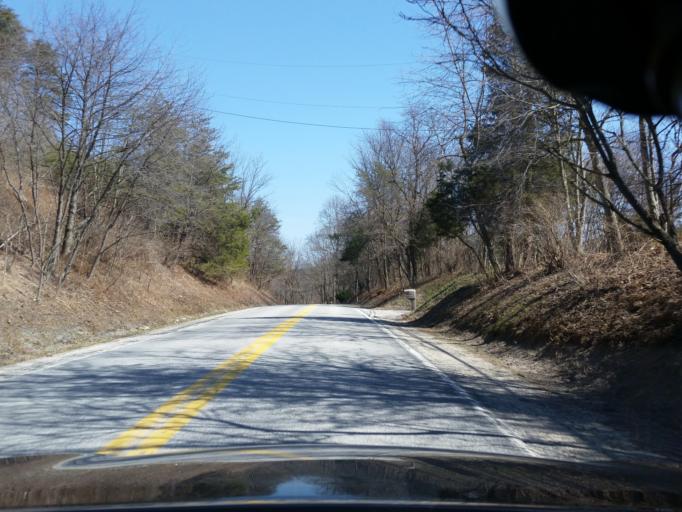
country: US
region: Pennsylvania
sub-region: Perry County
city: Marysville
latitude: 40.3277
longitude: -76.9856
